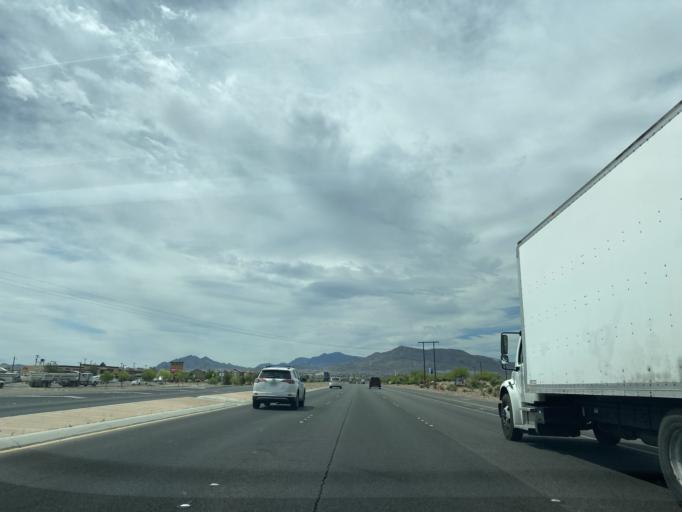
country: US
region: Nevada
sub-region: Clark County
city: Henderson
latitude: 36.0554
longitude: -114.9679
